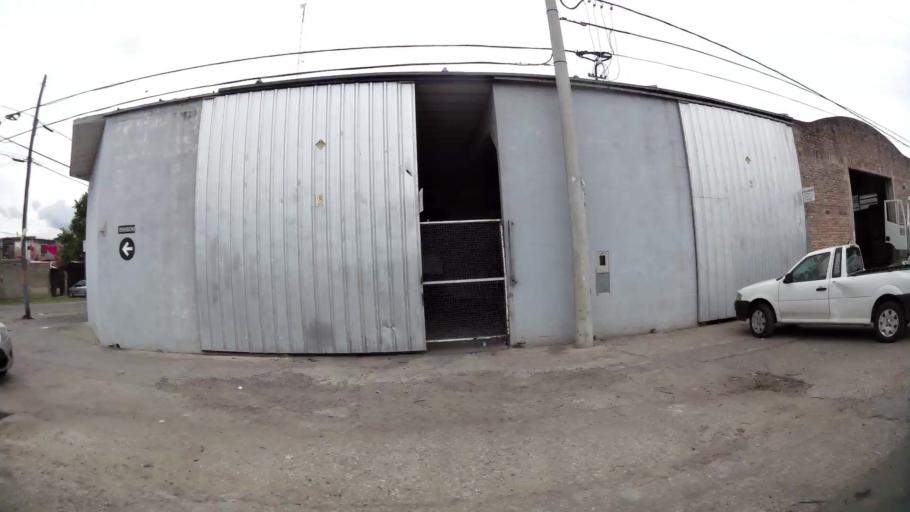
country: AR
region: Santa Fe
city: Gobernador Galvez
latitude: -33.0062
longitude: -60.6548
